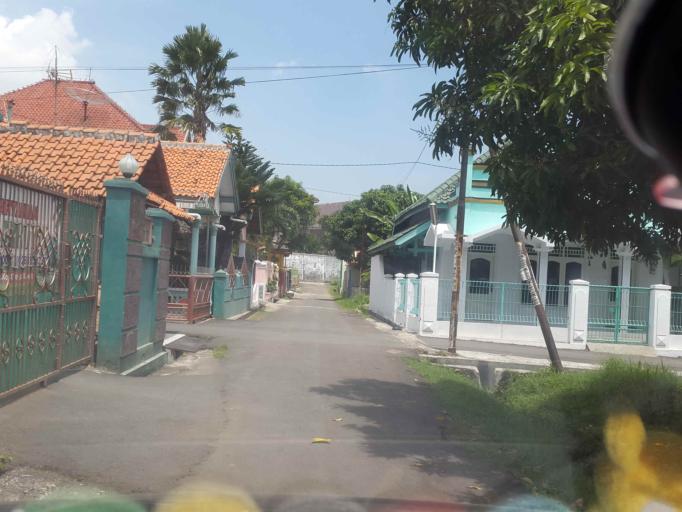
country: ID
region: Central Java
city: Tegal
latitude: -6.8683
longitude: 109.1448
